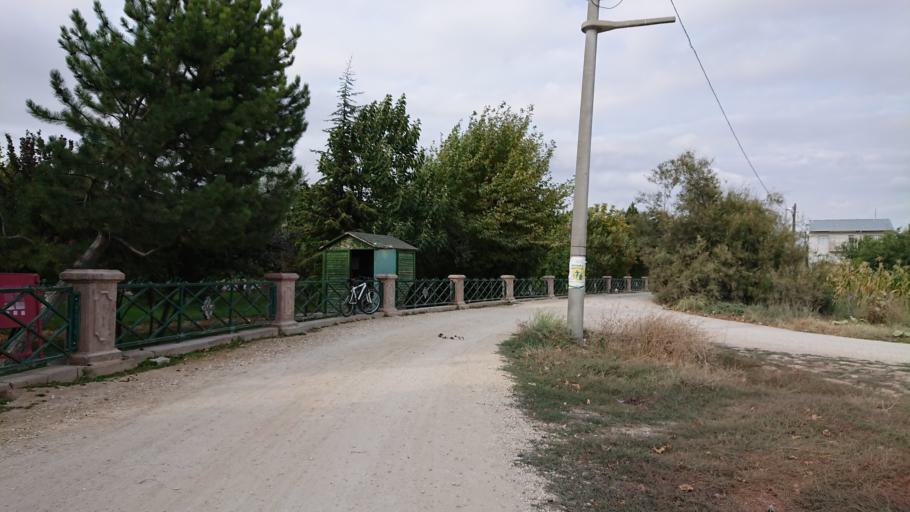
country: TR
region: Eskisehir
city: Eskisehir
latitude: 39.7644
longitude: 30.4864
